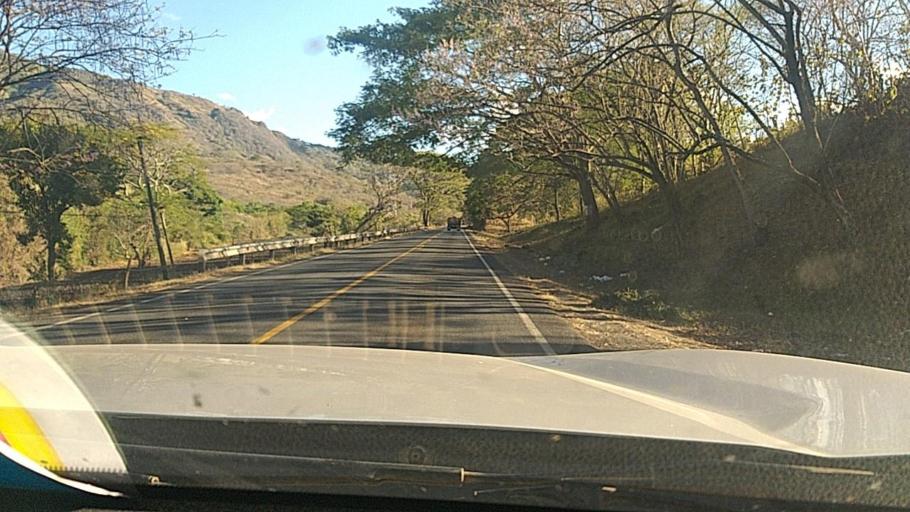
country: NI
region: Esteli
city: Condega
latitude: 13.2887
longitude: -86.3464
